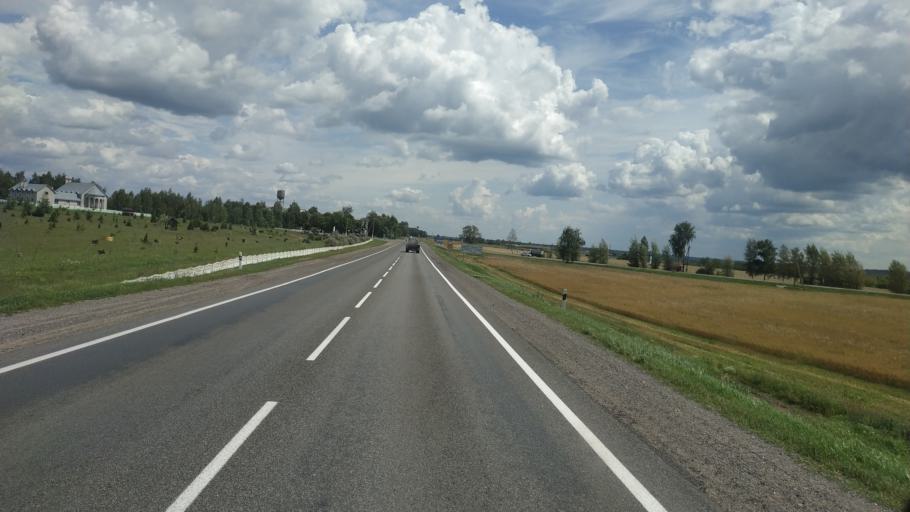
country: BY
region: Mogilev
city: Chavusy
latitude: 53.8020
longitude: 30.9494
